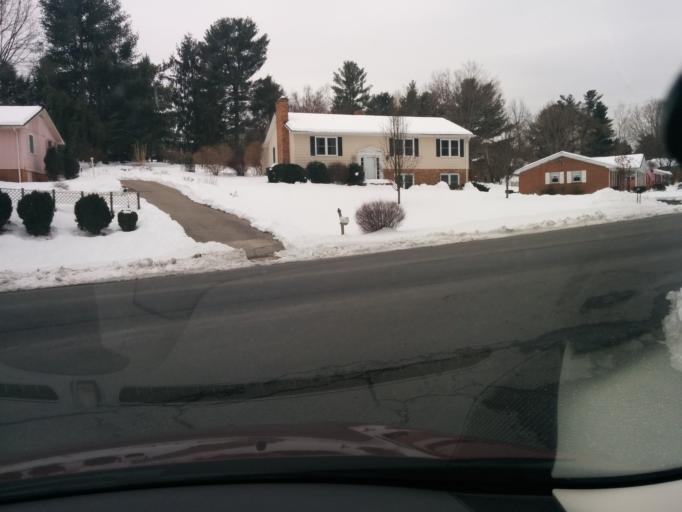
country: US
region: Virginia
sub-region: City of Lexington
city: Lexington
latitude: 37.7694
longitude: -79.4520
